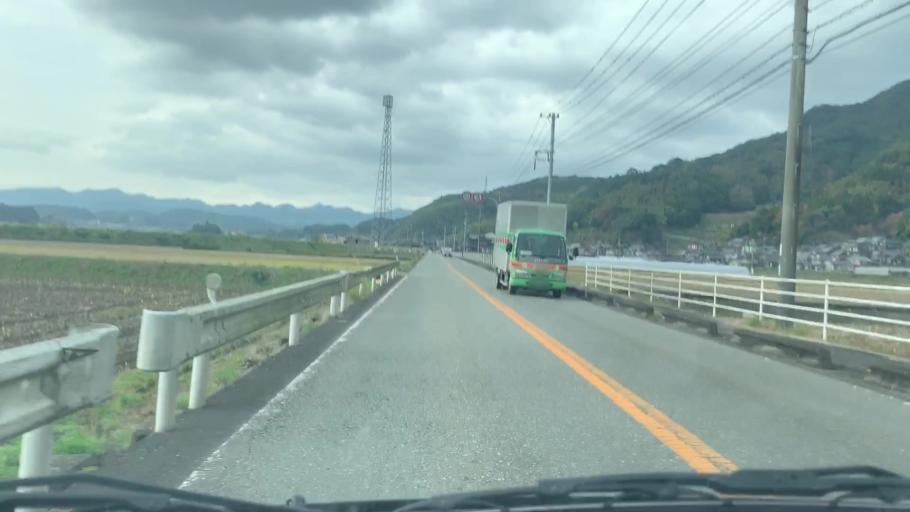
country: JP
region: Saga Prefecture
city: Ureshinomachi-shimojuku
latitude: 33.1368
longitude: 130.0193
